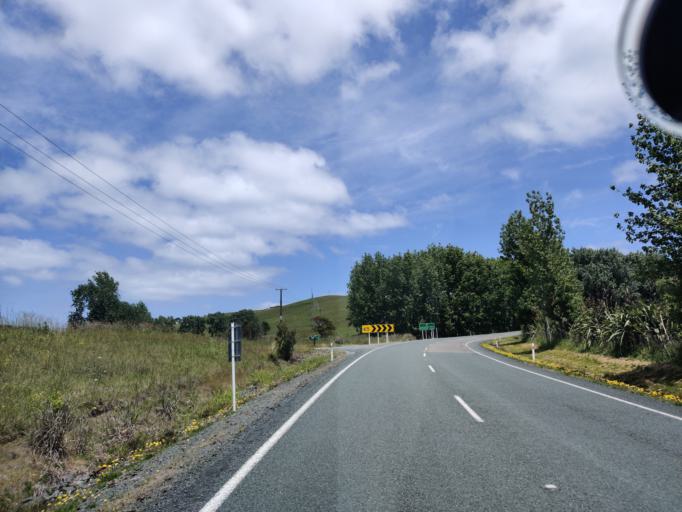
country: NZ
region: Auckland
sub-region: Auckland
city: Wellsford
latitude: -36.3796
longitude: 174.4509
